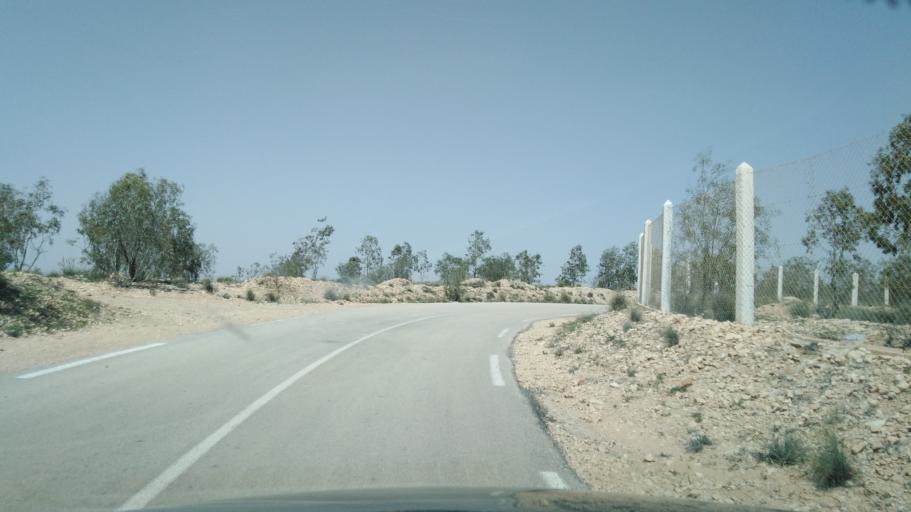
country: TN
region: Safaqis
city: Sfax
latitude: 34.7076
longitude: 10.5227
